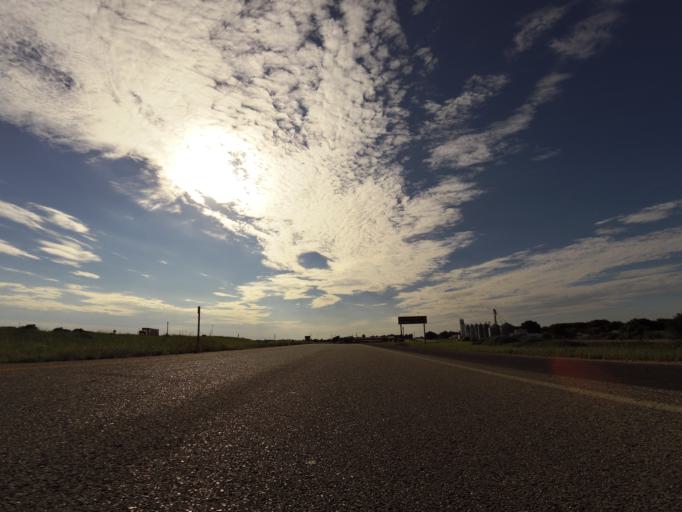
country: US
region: Kansas
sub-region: Reno County
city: Haven
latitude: 37.9361
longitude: -97.8632
